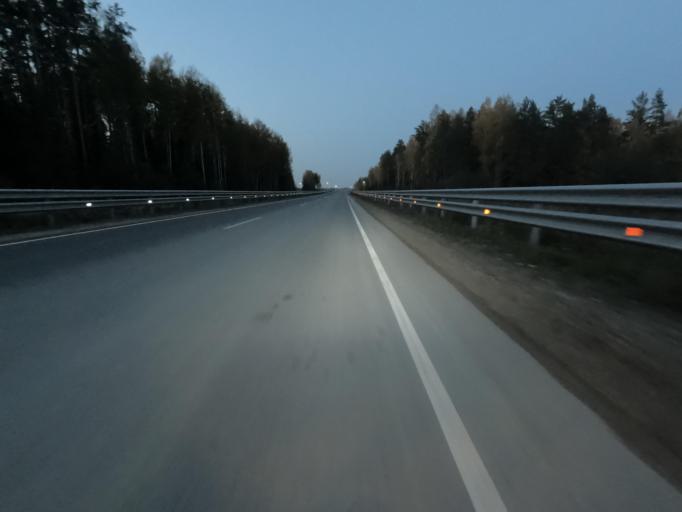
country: RU
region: Leningrad
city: Lyuban'
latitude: 59.1936
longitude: 31.2531
